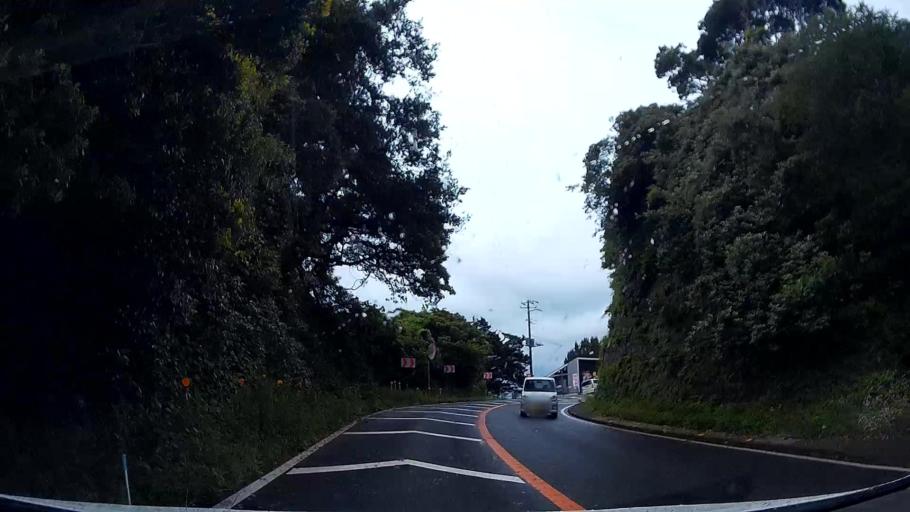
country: JP
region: Shizuoka
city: Shimoda
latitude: 34.7058
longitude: 138.9782
